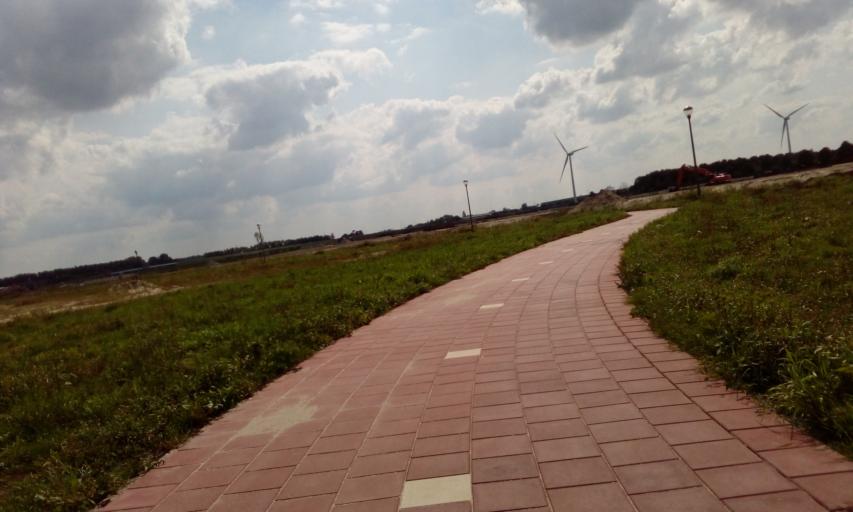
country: NL
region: South Holland
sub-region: Gemeente Waddinxveen
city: Waddinxveen
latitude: 52.0295
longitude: 4.6435
